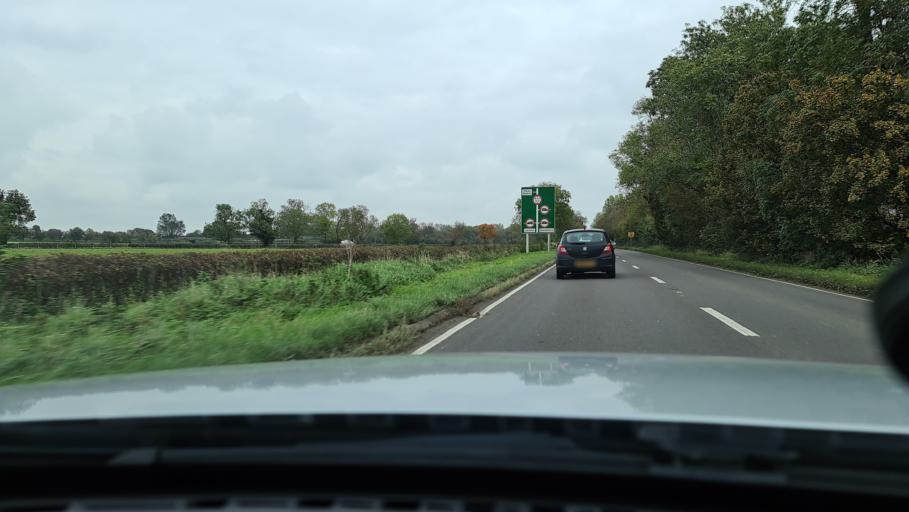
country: GB
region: England
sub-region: Oxfordshire
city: Bicester
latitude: 51.8778
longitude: -1.1035
